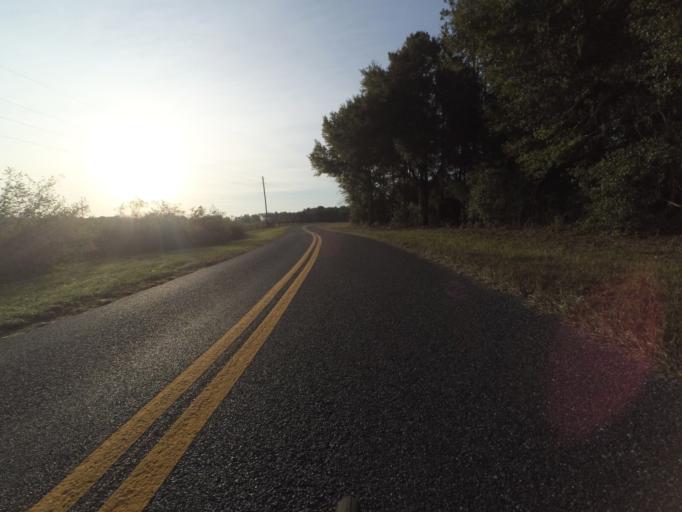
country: US
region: Florida
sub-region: Lake County
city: Umatilla
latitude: 28.9408
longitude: -81.7044
